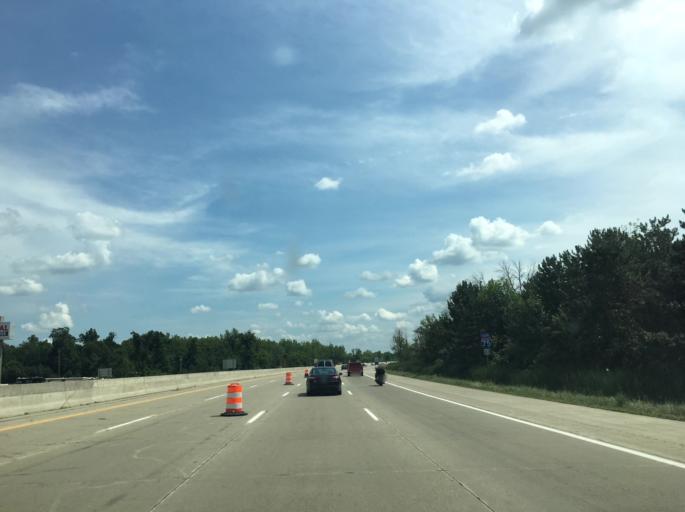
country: US
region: Michigan
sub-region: Saginaw County
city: Birch Run
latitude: 43.2449
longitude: -83.7709
